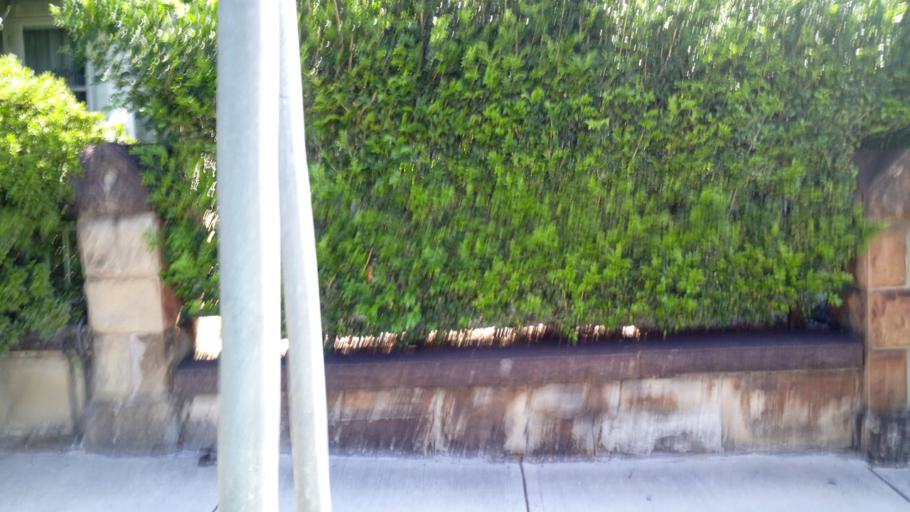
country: AU
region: New South Wales
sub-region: Waverley
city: Bondi Junction
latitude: -33.8915
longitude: 151.2537
